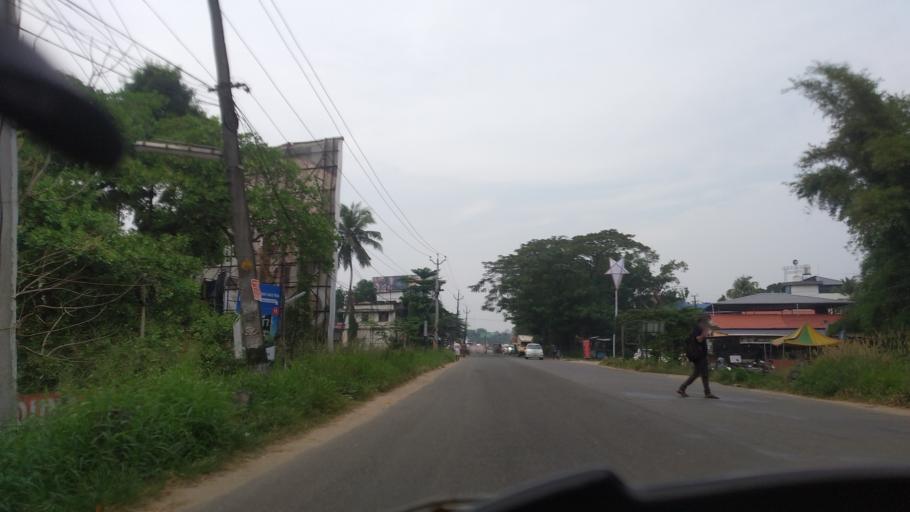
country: IN
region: Kerala
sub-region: Ernakulam
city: Elur
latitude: 10.0590
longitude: 76.2901
